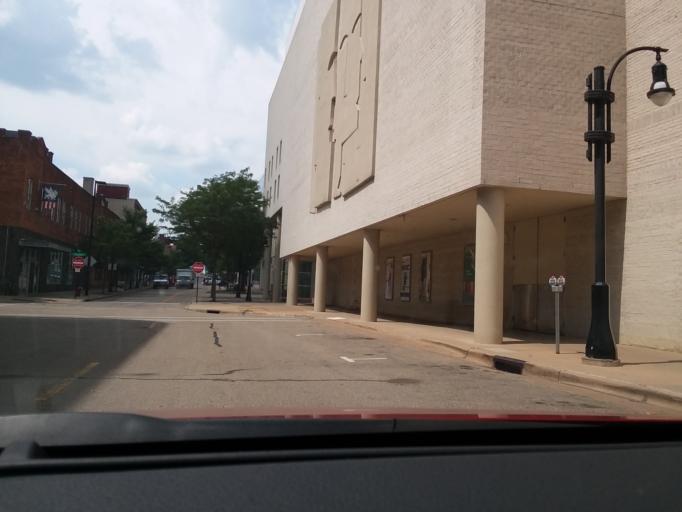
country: US
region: Wisconsin
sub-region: Dane County
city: Madison
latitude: 43.0739
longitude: -89.3888
